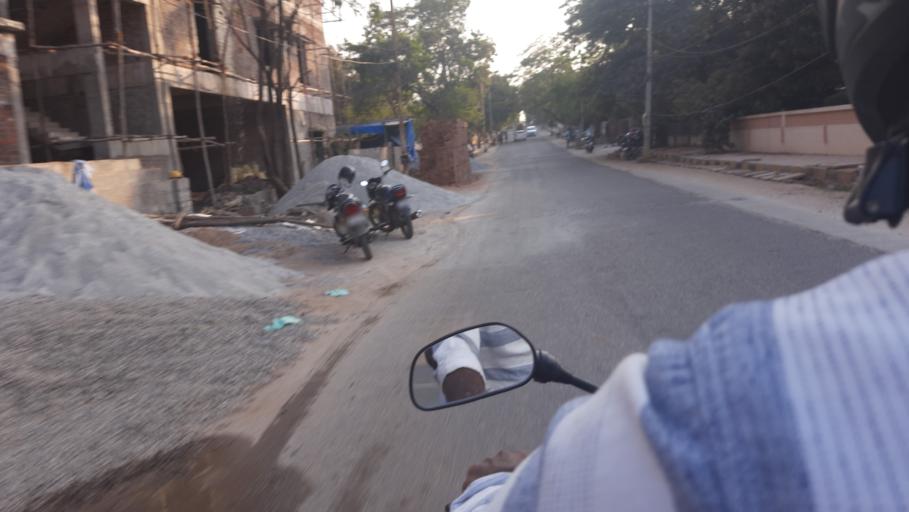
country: IN
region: Telangana
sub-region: Rangareddi
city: Secunderabad
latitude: 17.4885
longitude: 78.5491
